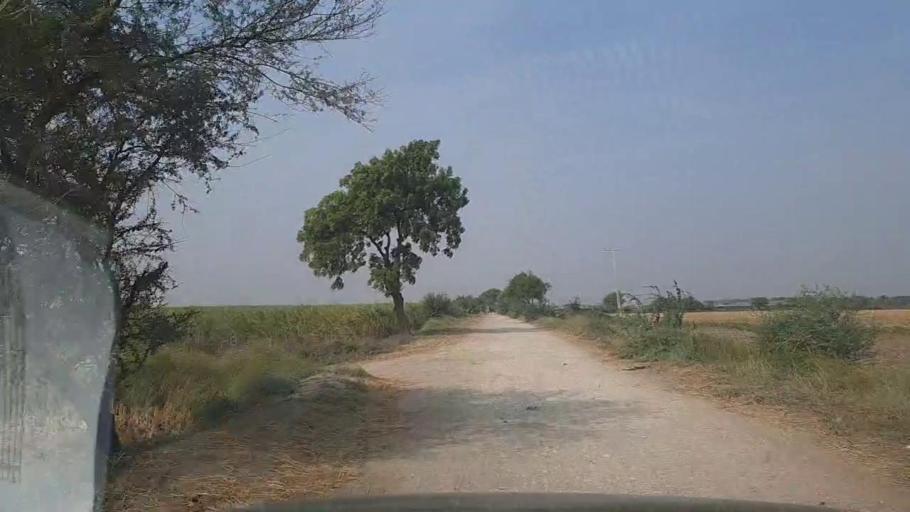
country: PK
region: Sindh
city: Bulri
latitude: 24.9715
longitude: 68.3097
